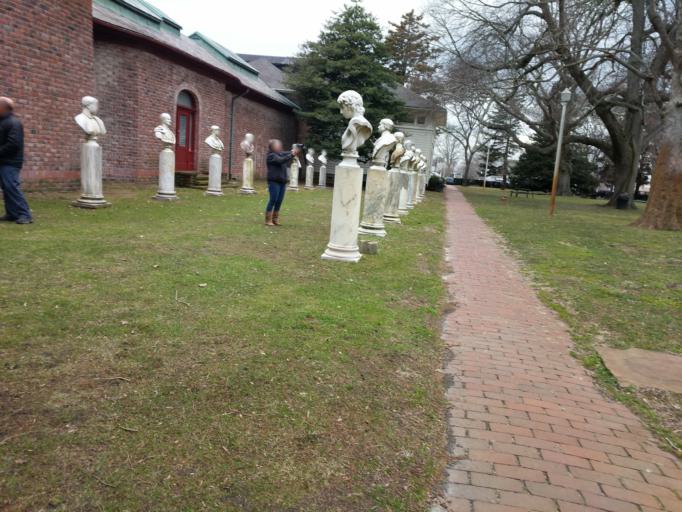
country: US
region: New York
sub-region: Suffolk County
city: Southampton
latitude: 40.8841
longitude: -72.3904
